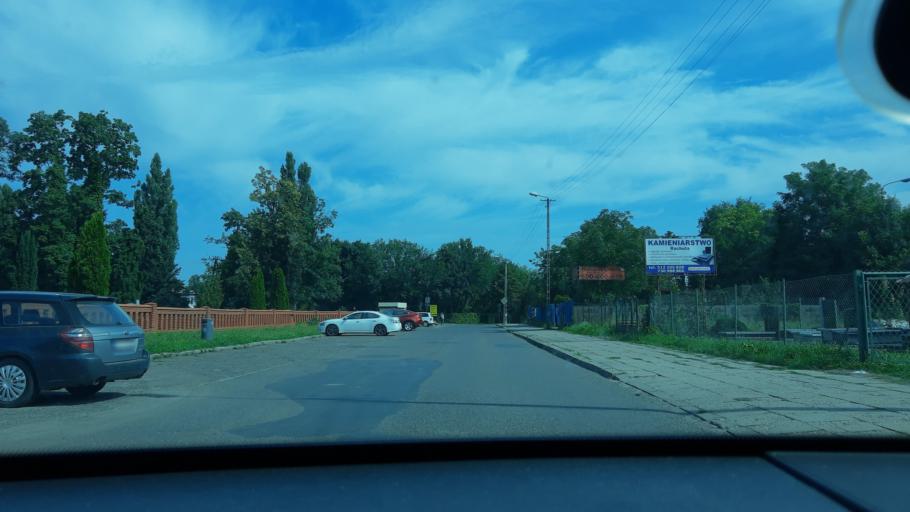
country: PL
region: Lodz Voivodeship
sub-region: Powiat sieradzki
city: Sieradz
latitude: 51.5987
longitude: 18.7283
